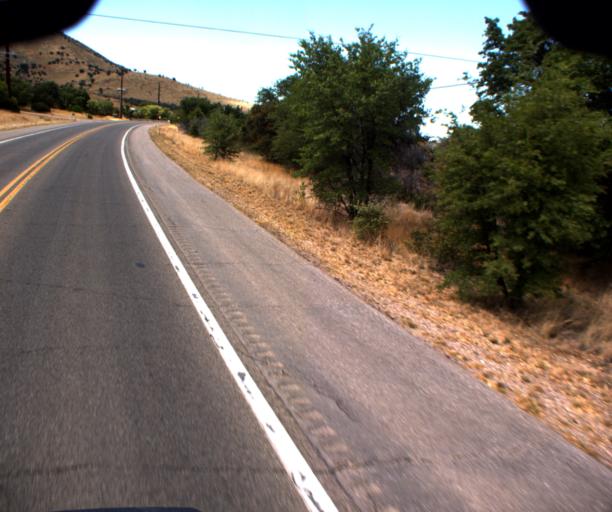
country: US
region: Arizona
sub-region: Cochise County
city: Sierra Vista Southeast
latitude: 31.3973
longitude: -110.2384
